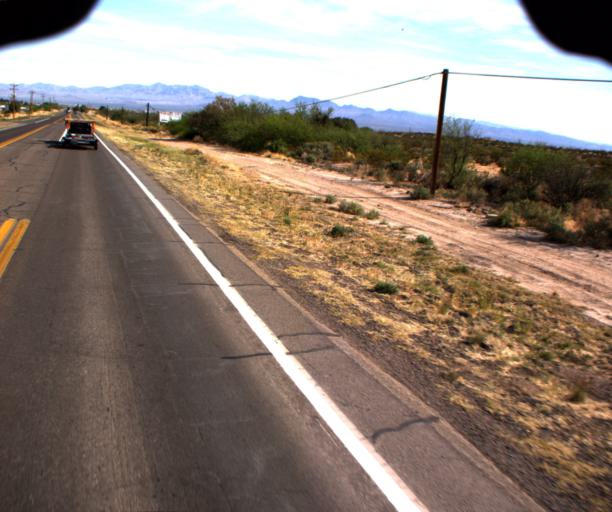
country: US
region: Arizona
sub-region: Graham County
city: Cactus Flat
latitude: 32.7502
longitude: -109.7163
